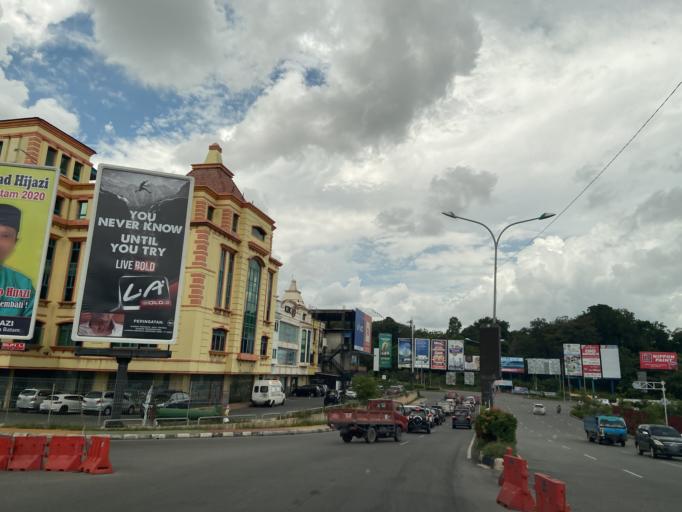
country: SG
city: Singapore
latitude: 1.1321
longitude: 104.0170
